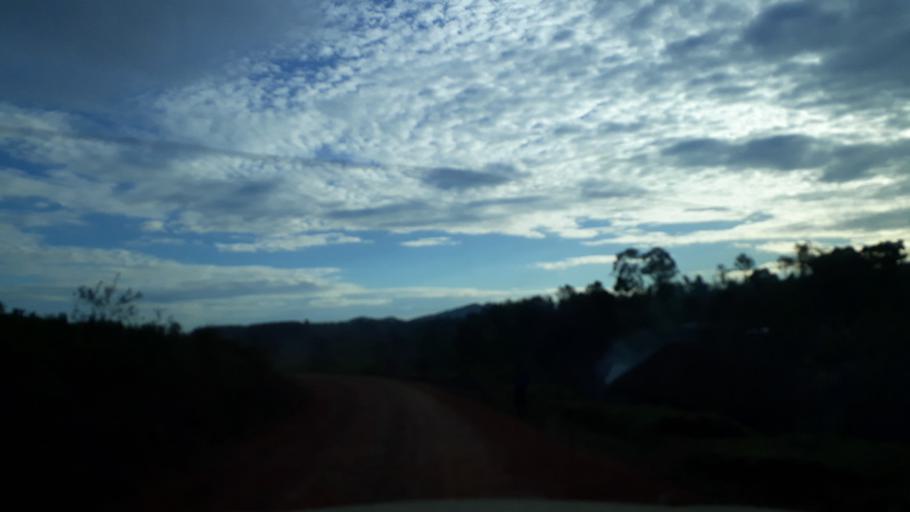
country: UG
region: Northern Region
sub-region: Zombo District
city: Paidha
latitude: 2.2250
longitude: 30.8107
